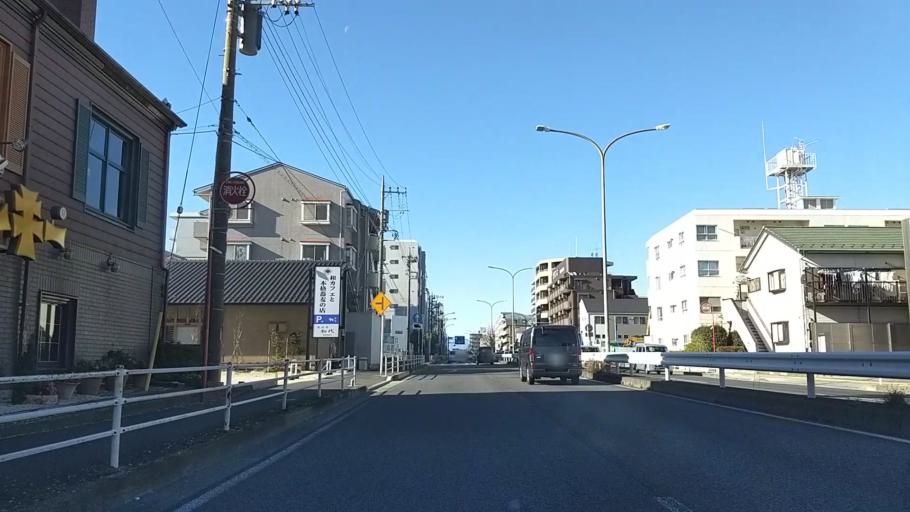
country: JP
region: Tokyo
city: Chofugaoka
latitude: 35.5770
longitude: 139.5812
